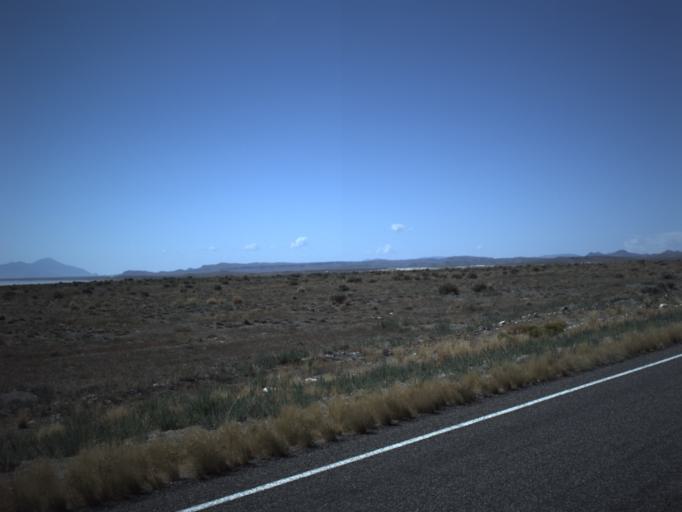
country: US
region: Utah
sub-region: Millard County
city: Delta
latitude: 39.0806
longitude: -113.1969
